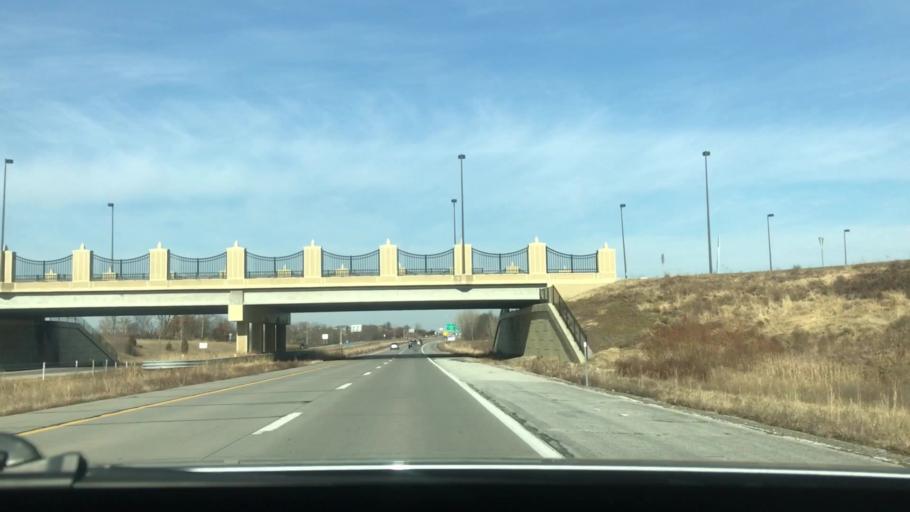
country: US
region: Missouri
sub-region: Clay County
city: Gladstone
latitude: 39.2887
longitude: -94.5851
